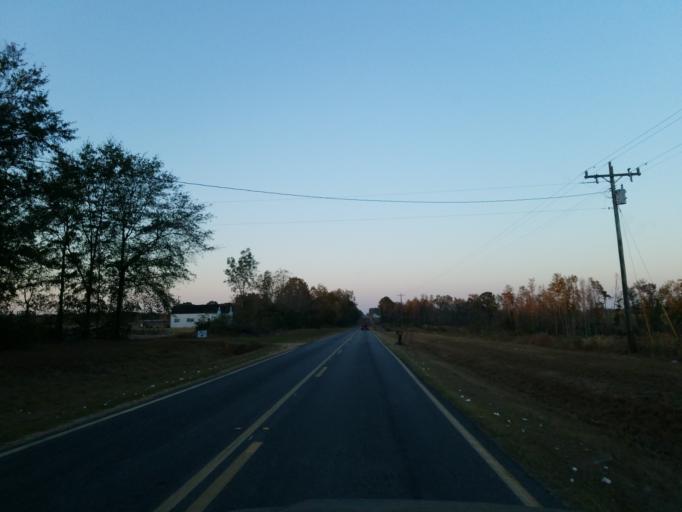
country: US
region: Georgia
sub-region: Ben Hill County
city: Fitzgerald
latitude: 31.7106
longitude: -83.3850
